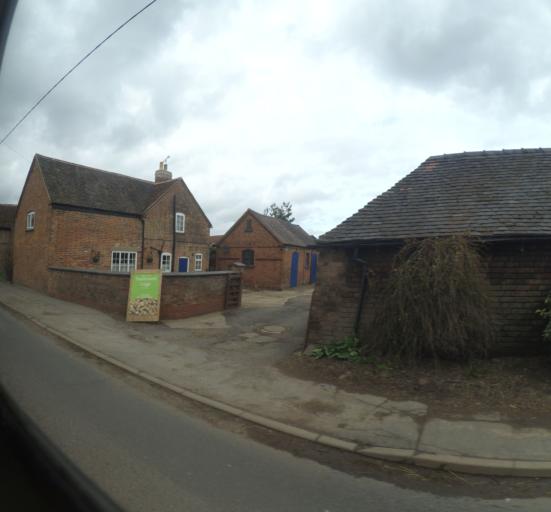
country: GB
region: England
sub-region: Warwickshire
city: Brandon
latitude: 52.4086
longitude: -1.3605
